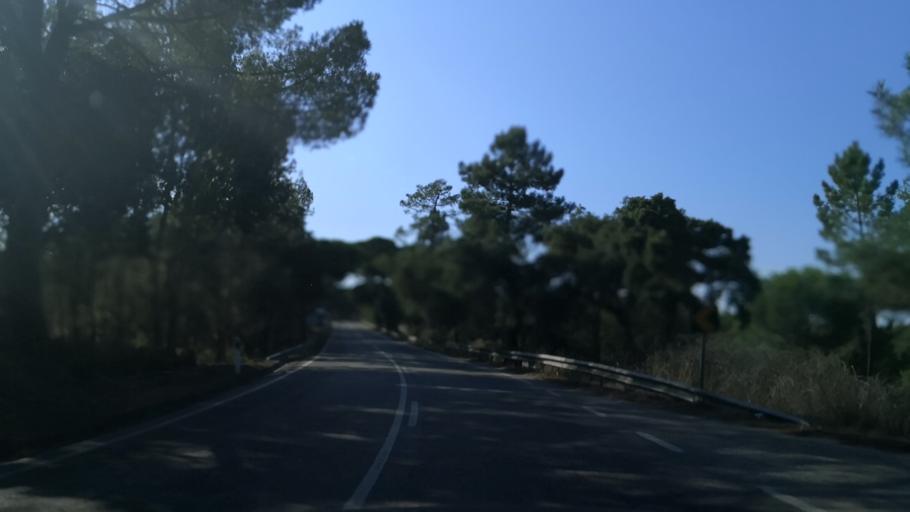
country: PT
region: Santarem
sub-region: Coruche
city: Coruche
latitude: 38.9764
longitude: -8.5407
